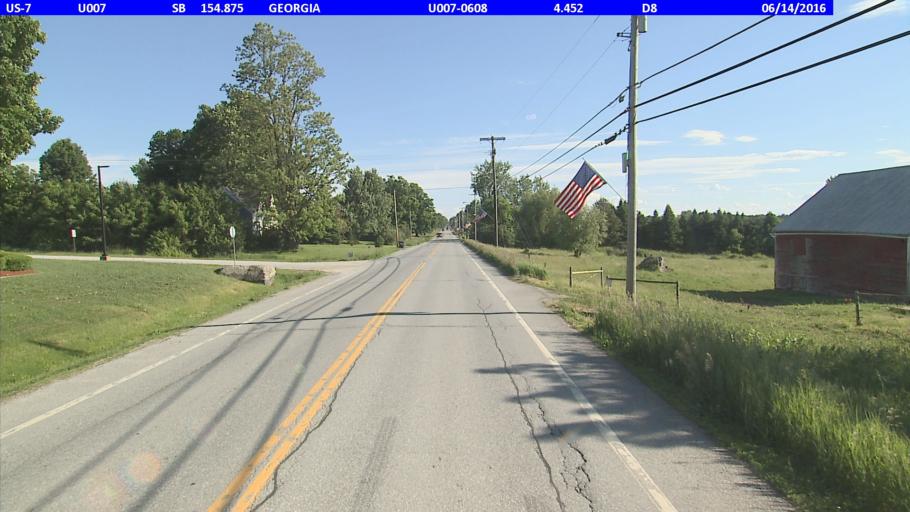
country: US
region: Vermont
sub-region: Franklin County
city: Saint Albans
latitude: 44.7354
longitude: -73.1160
